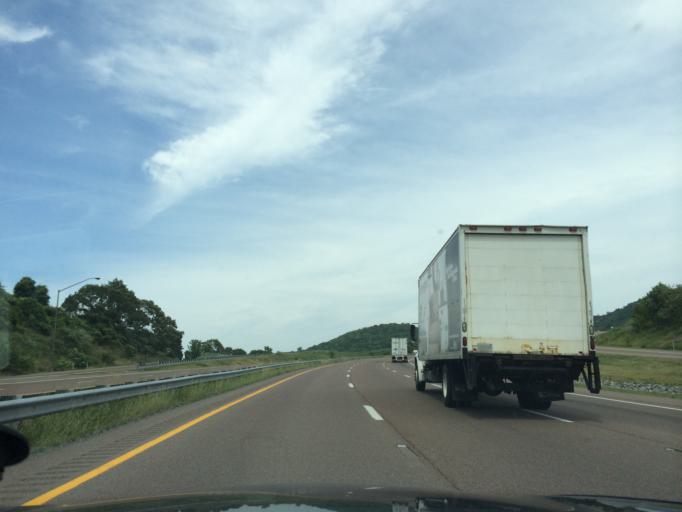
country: US
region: Maryland
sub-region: Allegany County
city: Cumberland
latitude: 39.6923
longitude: -78.6547
